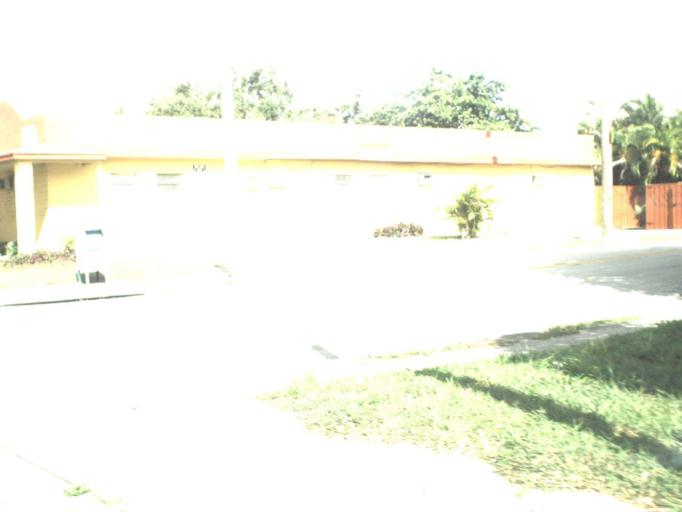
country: US
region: Florida
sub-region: Miami-Dade County
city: West Miami
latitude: 25.7721
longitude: -80.2497
